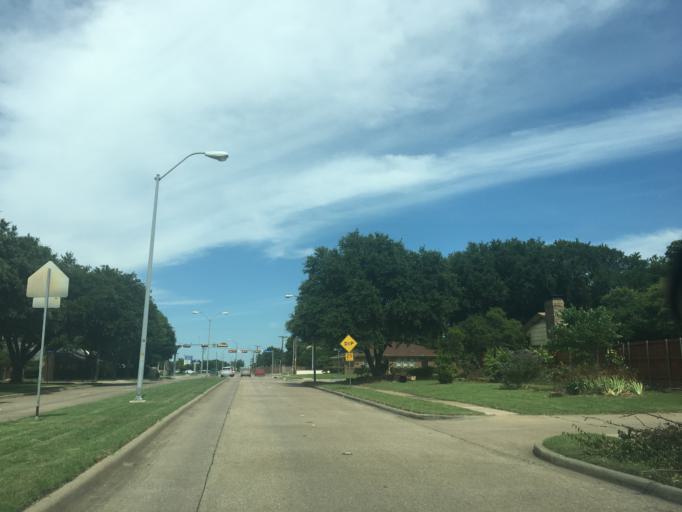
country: US
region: Texas
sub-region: Dallas County
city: Richardson
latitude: 32.9386
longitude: -96.7014
